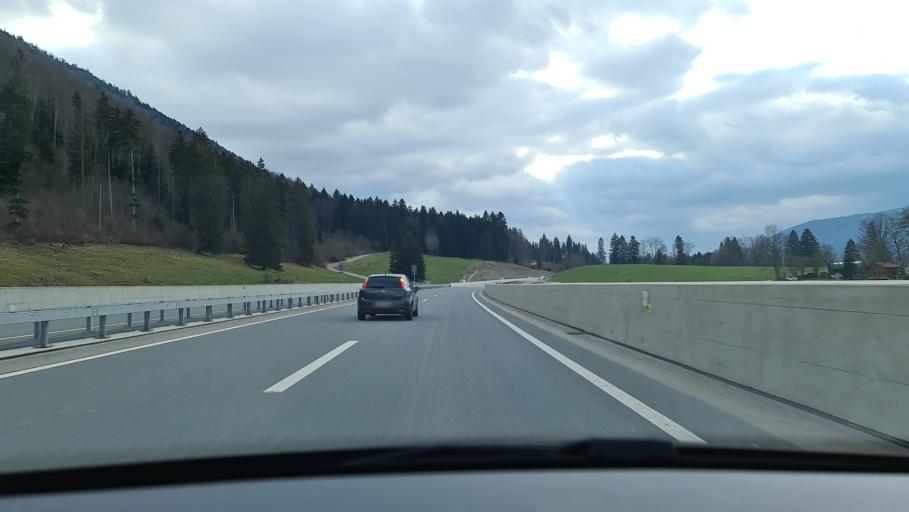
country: CH
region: Bern
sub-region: Jura bernois
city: Court
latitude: 47.2327
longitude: 7.3318
